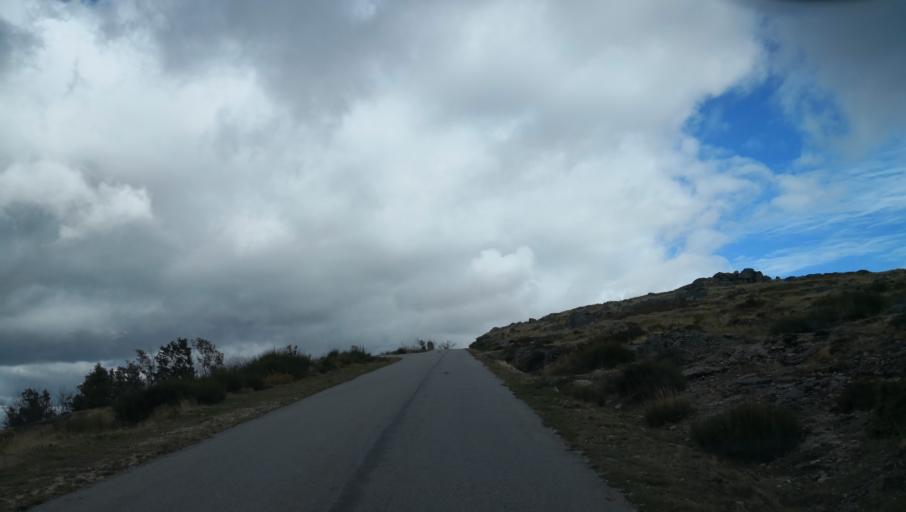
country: PT
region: Vila Real
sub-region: Vila Real
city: Vila Real
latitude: 41.3738
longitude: -7.8303
